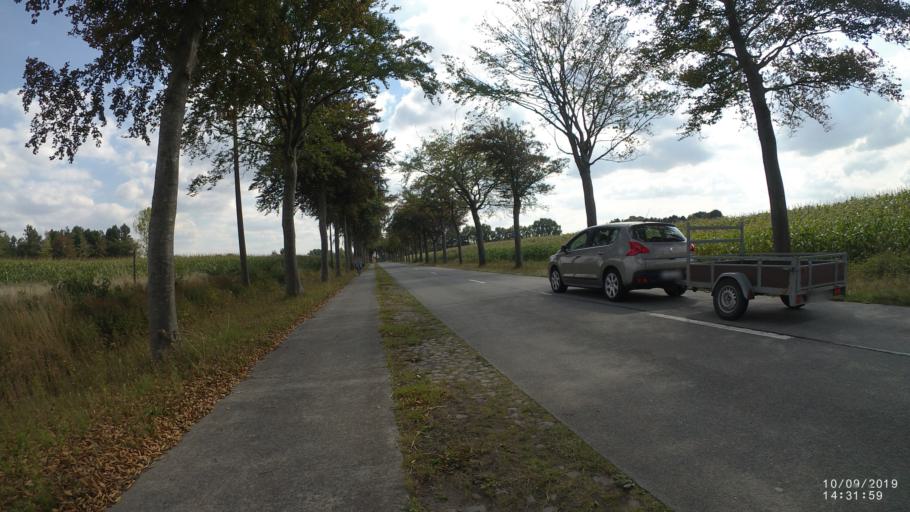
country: BE
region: Flanders
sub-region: Provincie Oost-Vlaanderen
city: Assenede
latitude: 51.2045
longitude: 3.6850
